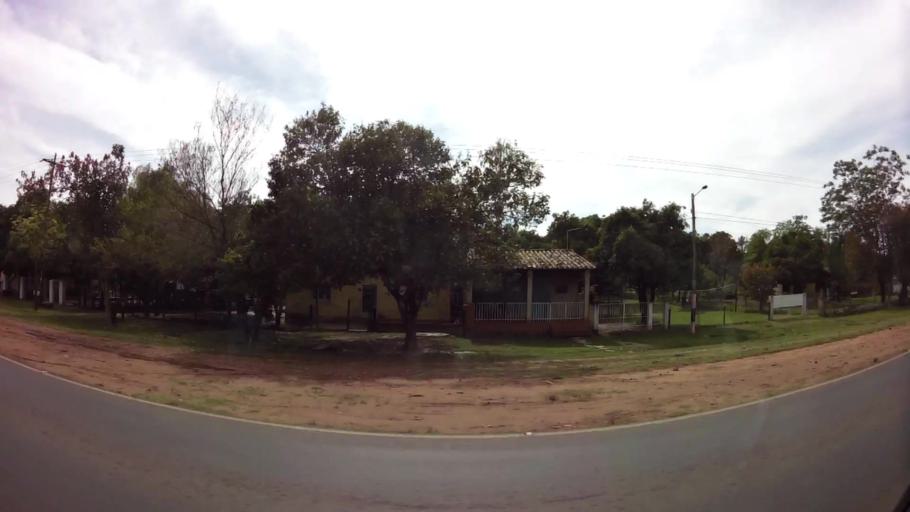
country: PY
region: Presidente Hayes
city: Villa Hayes
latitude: -25.1142
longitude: -57.4887
